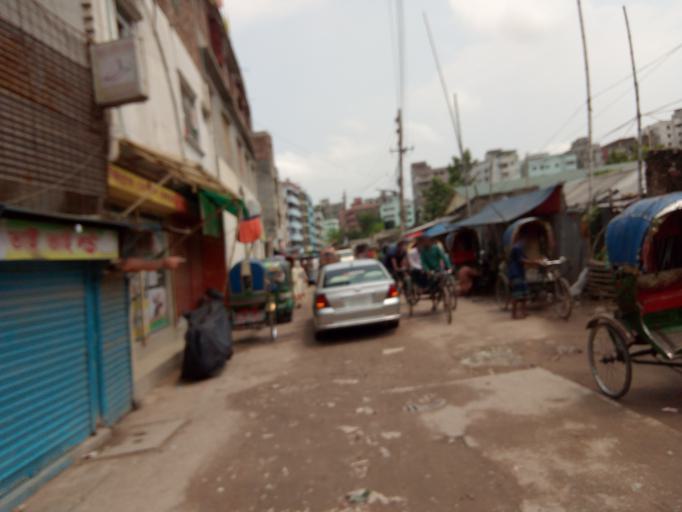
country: BD
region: Dhaka
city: Azimpur
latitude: 23.7432
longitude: 90.3633
